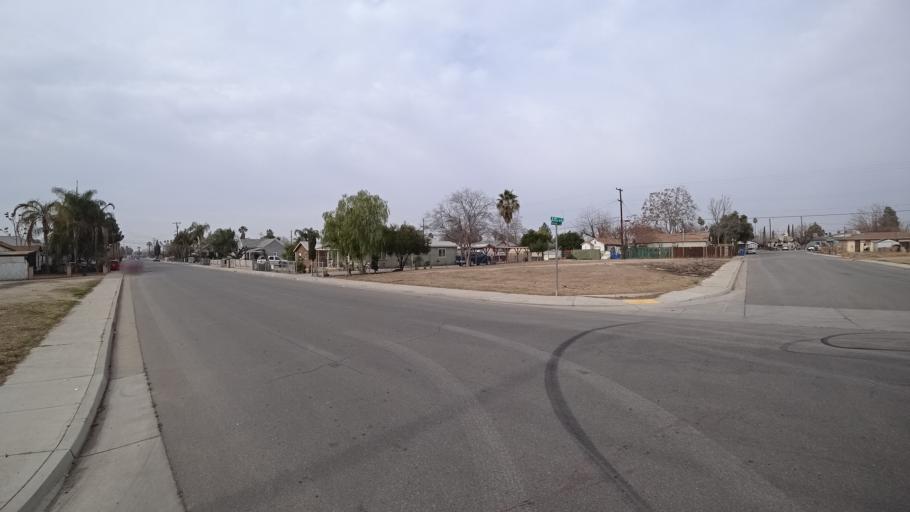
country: US
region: California
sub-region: Kern County
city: Bakersfield
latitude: 35.3655
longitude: -118.9971
